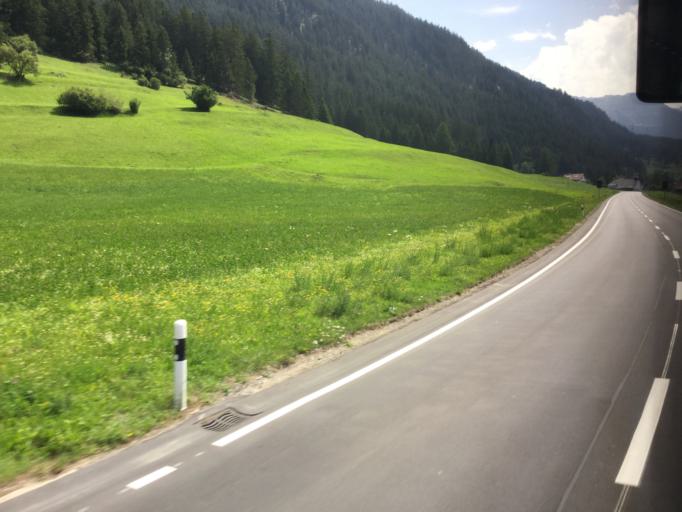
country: CH
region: Grisons
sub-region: Albula District
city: Tiefencastel
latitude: 46.6283
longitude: 9.5841
